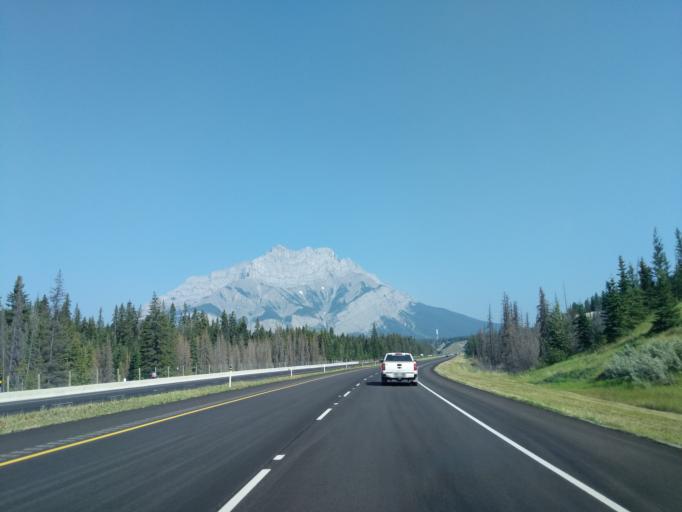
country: CA
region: Alberta
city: Banff
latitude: 51.1823
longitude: -115.4837
